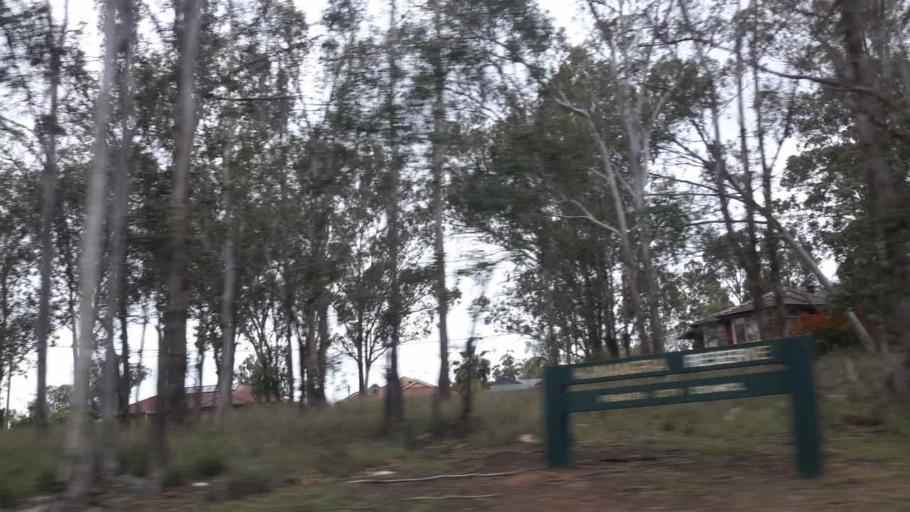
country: AU
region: New South Wales
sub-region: Penrith Municipality
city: Cambridge Park
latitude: -33.7478
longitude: 150.7143
